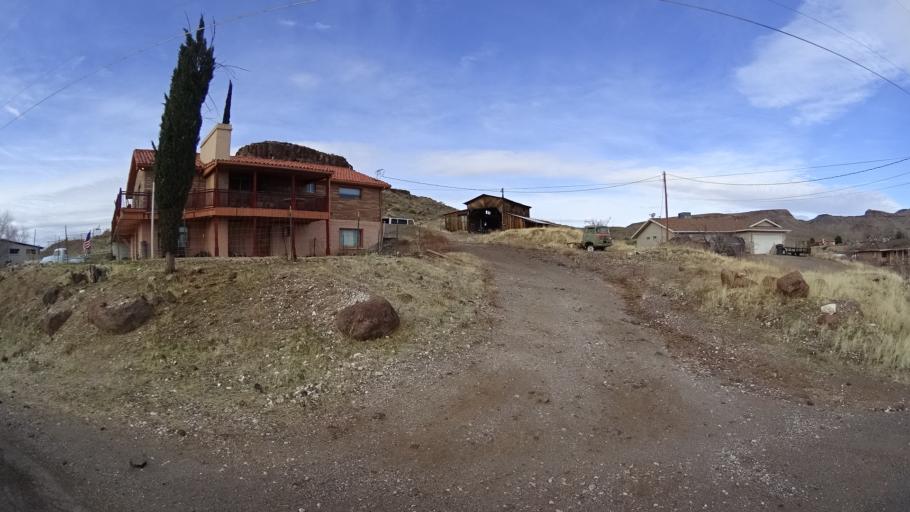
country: US
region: Arizona
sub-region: Mohave County
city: Kingman
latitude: 35.2253
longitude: -114.0485
